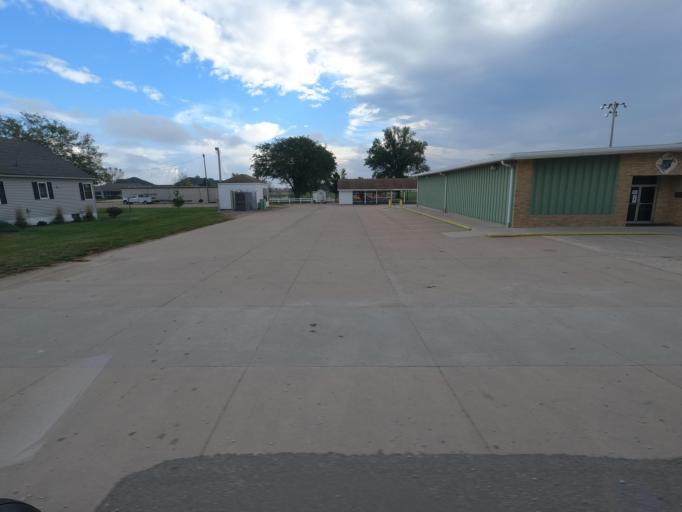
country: US
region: Iowa
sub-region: Henry County
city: Mount Pleasant
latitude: 40.7847
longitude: -91.6072
